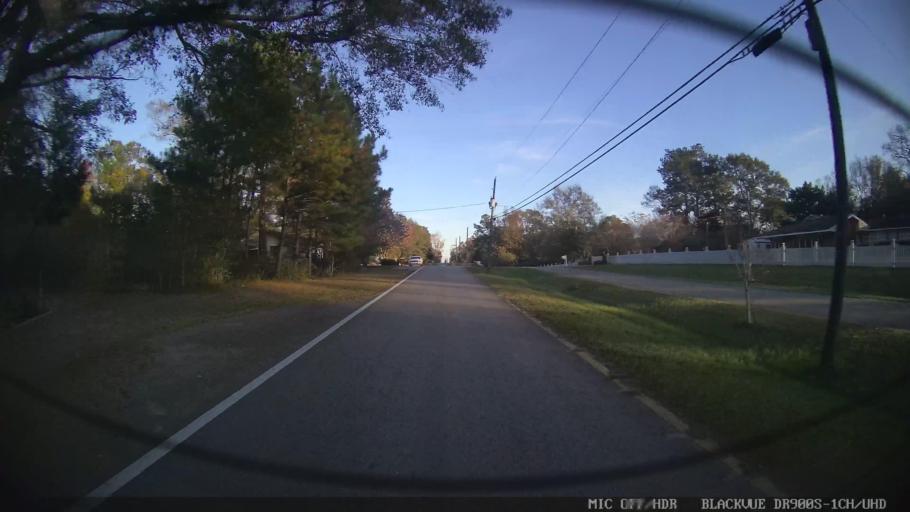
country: US
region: Mississippi
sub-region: Lamar County
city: Lumberton
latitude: 31.0043
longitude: -89.4600
